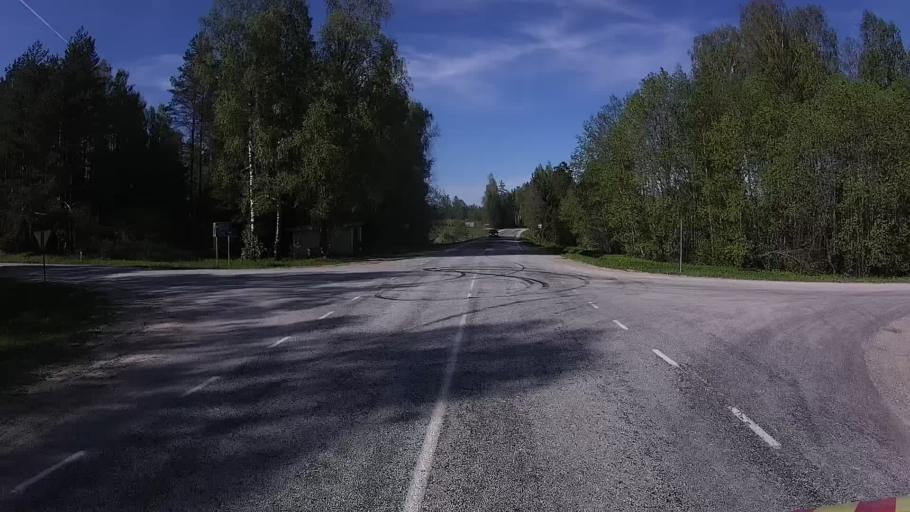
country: EE
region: Vorumaa
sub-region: Antsla vald
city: Vana-Antsla
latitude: 57.9964
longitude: 26.4950
